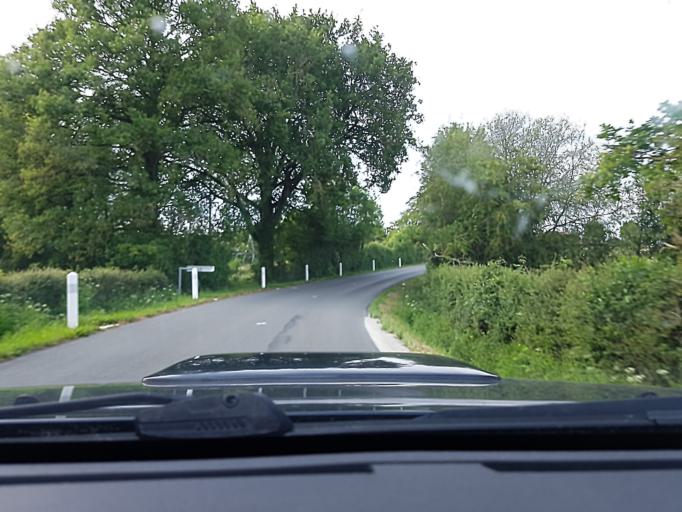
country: FR
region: Pays de la Loire
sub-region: Departement de la Vendee
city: Mache
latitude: 46.7902
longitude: -1.6632
